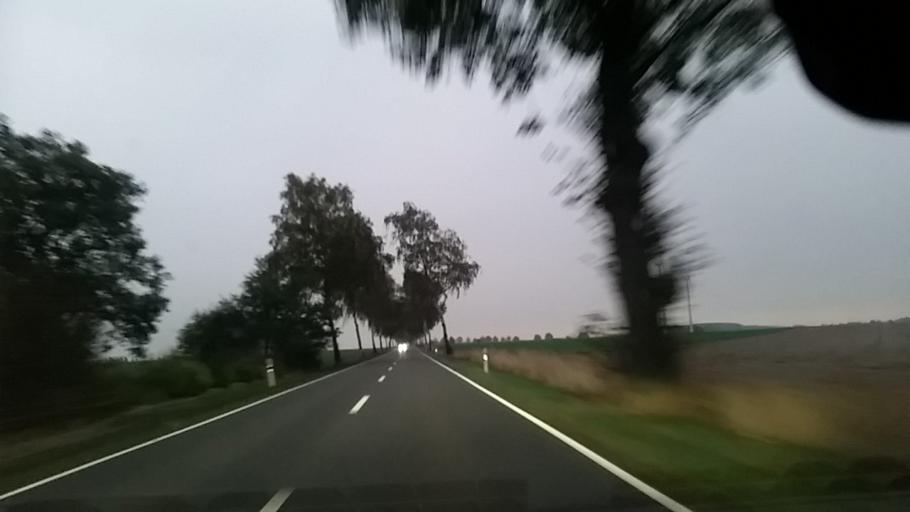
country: DE
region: Lower Saxony
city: Wittingen
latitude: 52.7580
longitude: 10.7121
